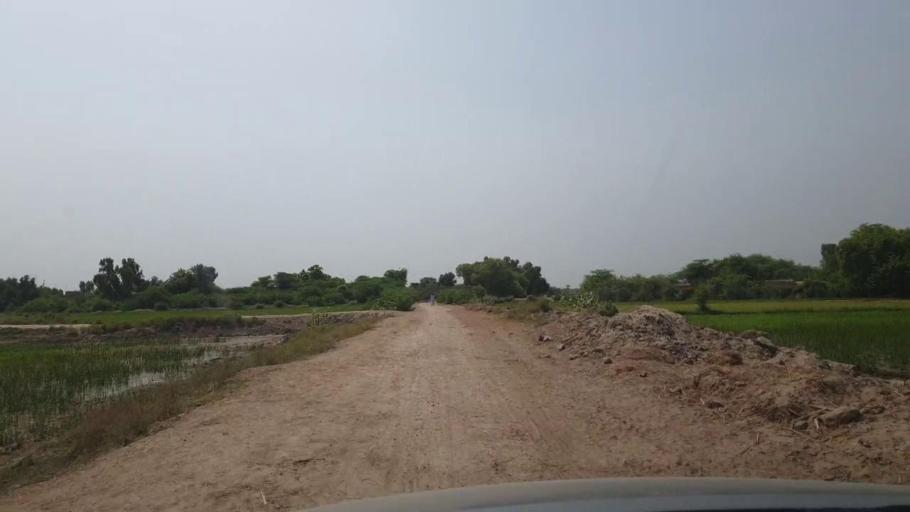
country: PK
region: Sindh
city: Madeji
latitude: 27.7980
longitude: 68.5404
